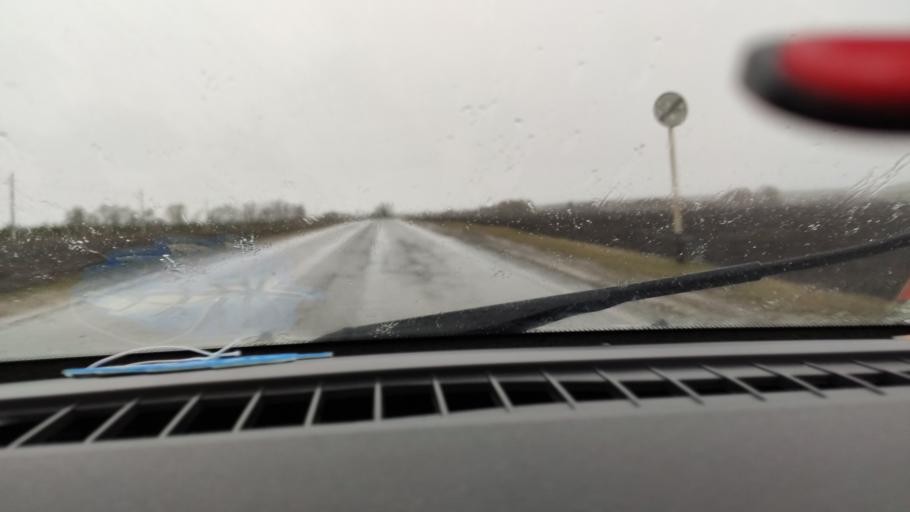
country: RU
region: Samara
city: Chelno-Vershiny
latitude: 54.7054
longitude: 51.1642
